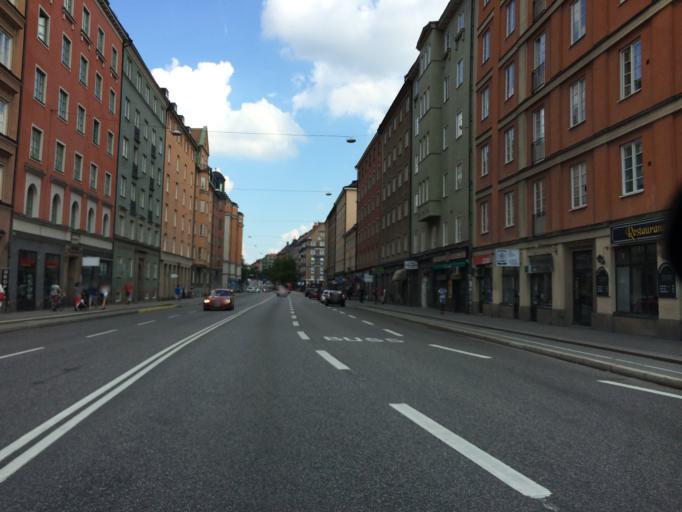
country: SE
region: Stockholm
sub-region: Stockholms Kommun
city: Stockholm
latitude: 59.3378
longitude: 18.0353
